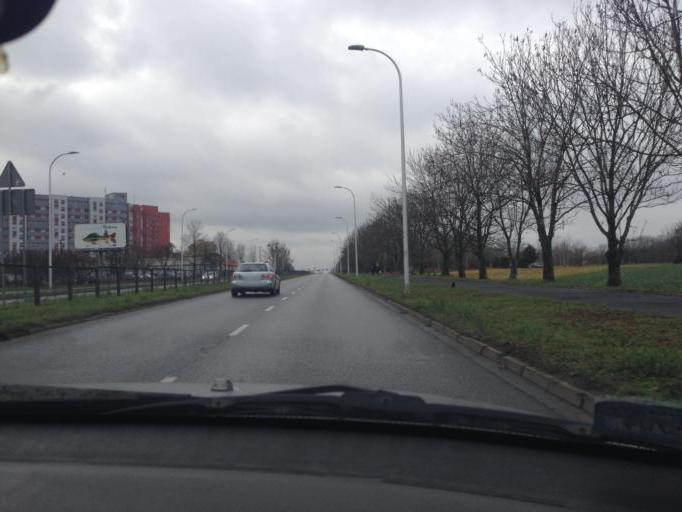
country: PL
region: Opole Voivodeship
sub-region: Powiat opolski
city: Opole
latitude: 50.6866
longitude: 17.9501
